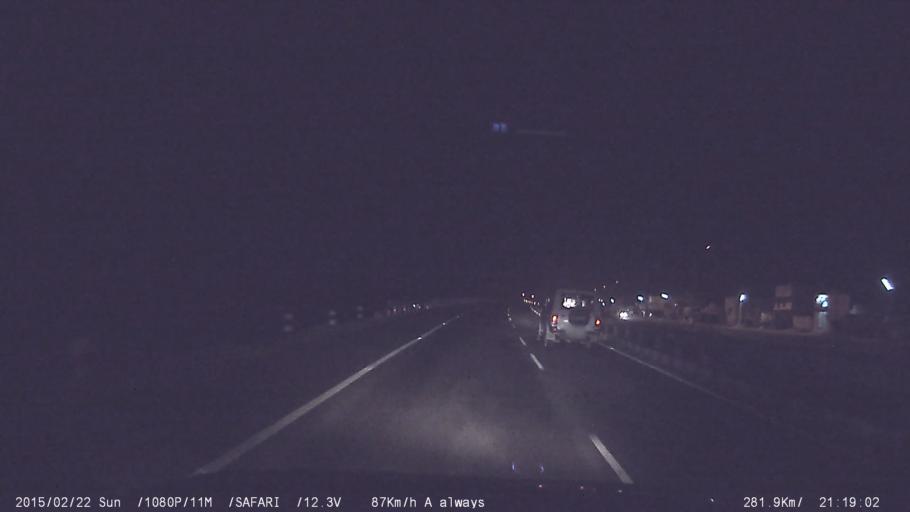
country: IN
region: Tamil Nadu
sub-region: Karur
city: Pallappatti
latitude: 10.8444
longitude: 77.9693
